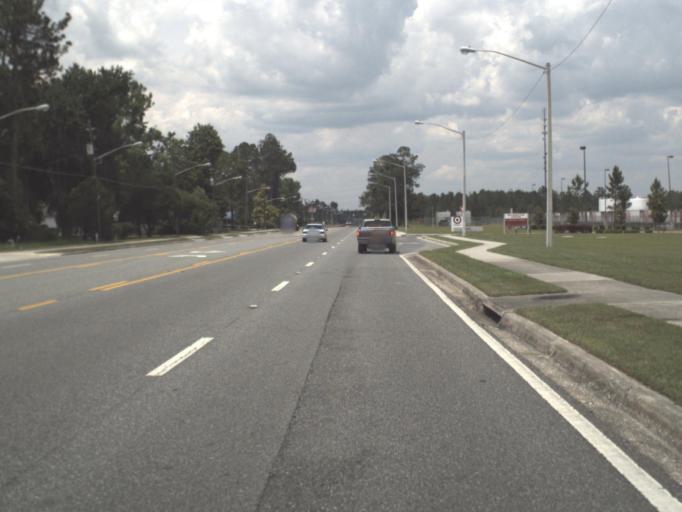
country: US
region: Florida
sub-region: Columbia County
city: Five Points
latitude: 30.2301
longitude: -82.6385
